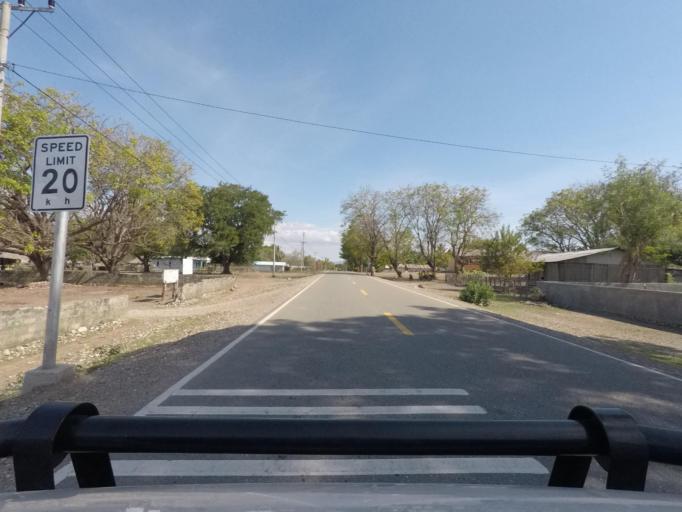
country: ID
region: East Nusa Tenggara
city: Atambua
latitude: -8.9008
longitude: 124.9992
